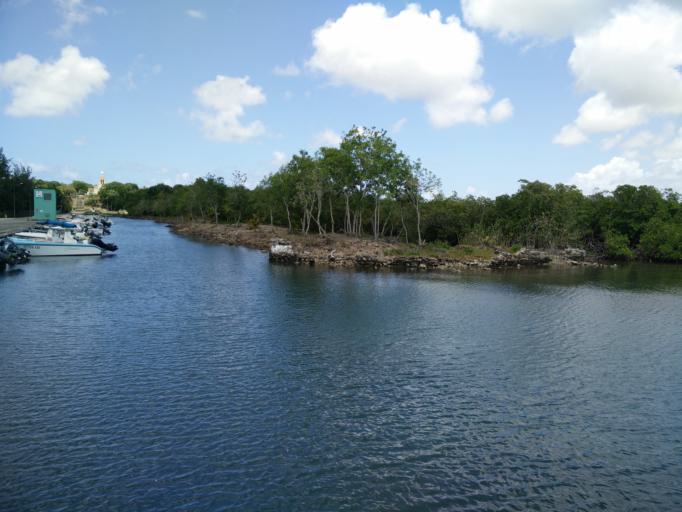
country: GP
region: Guadeloupe
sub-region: Guadeloupe
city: Petit-Canal
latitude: 16.3779
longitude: -61.4968
